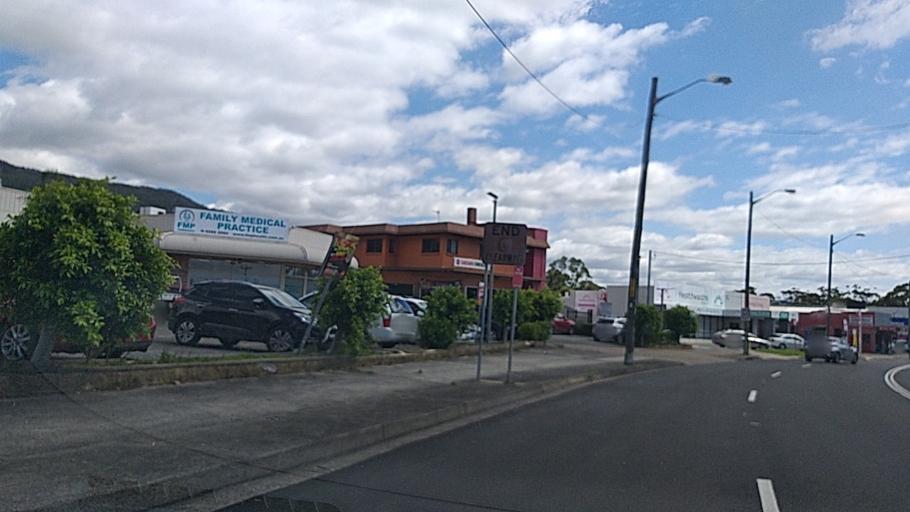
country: AU
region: New South Wales
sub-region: Wollongong
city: Corrimal
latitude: -34.3826
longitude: 150.8951
